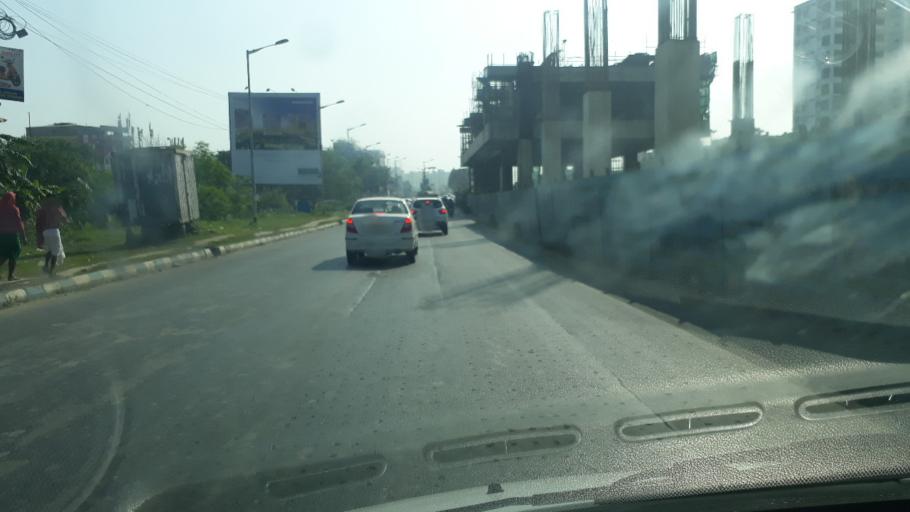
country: IN
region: West Bengal
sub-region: Kolkata
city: Kolkata
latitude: 22.5058
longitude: 88.4012
